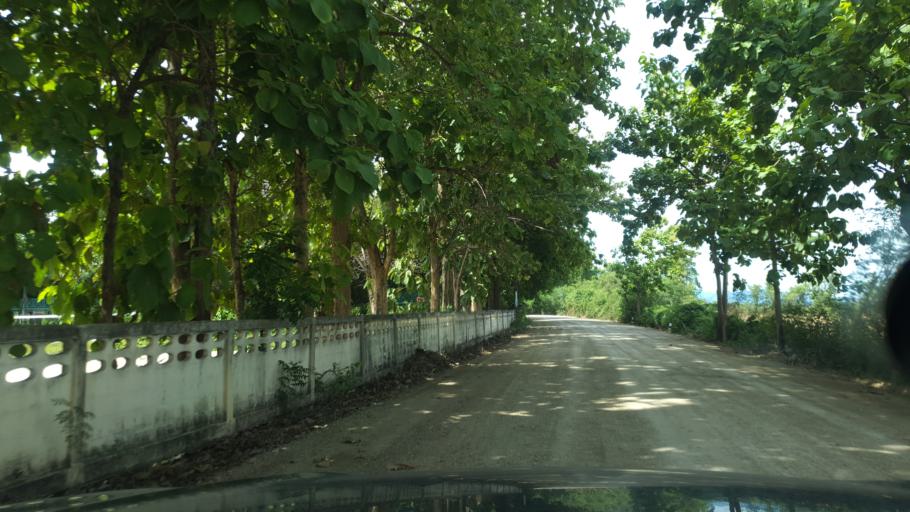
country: TH
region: Sukhothai
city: Sawankhalok
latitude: 17.2145
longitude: 99.7182
